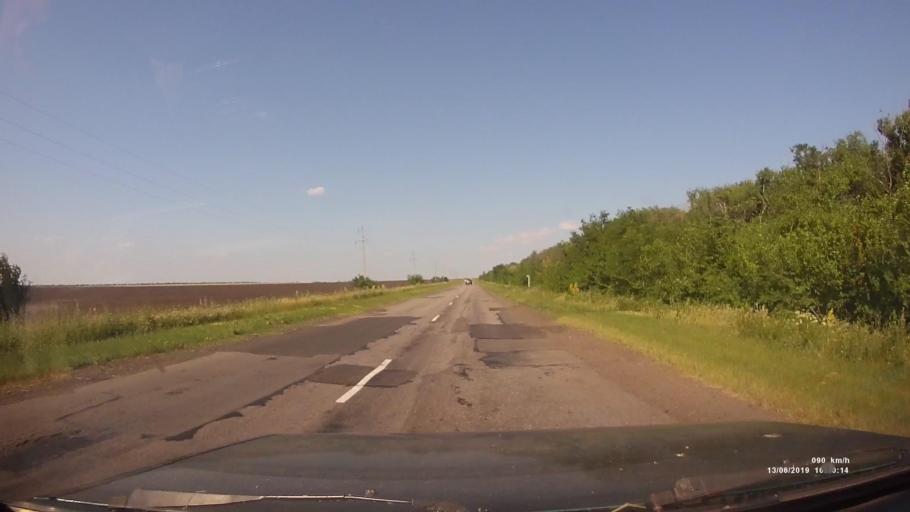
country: RU
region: Rostov
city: Kazanskaya
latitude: 49.8365
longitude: 41.2305
